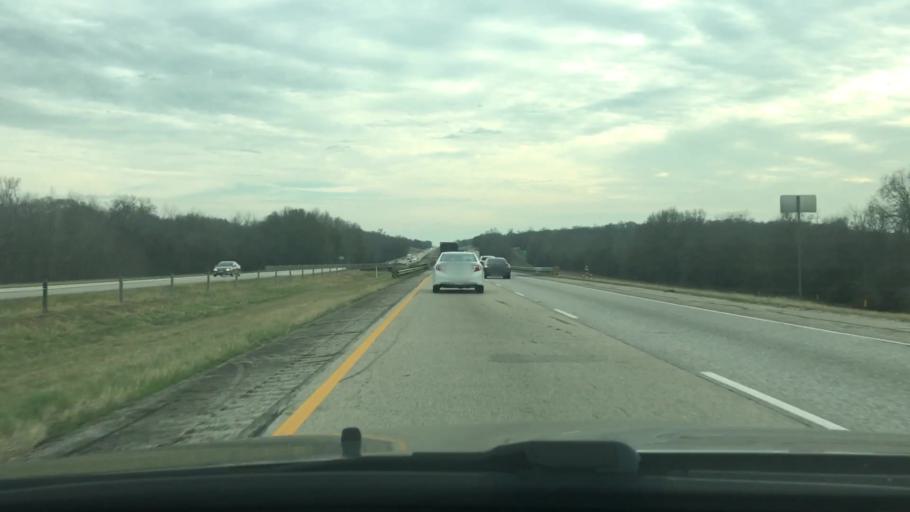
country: US
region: Texas
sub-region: Leon County
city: Centerville
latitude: 31.1905
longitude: -95.9925
